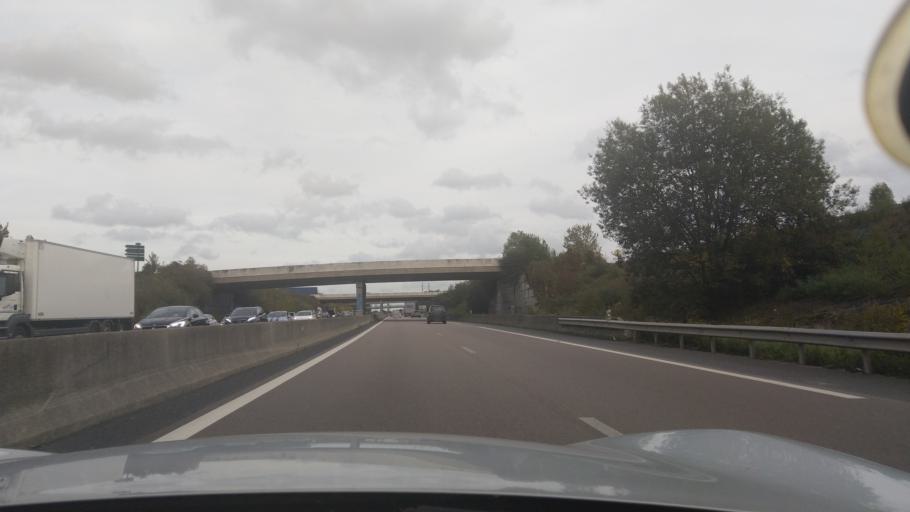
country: FR
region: Ile-de-France
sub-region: Departement du Val-d'Oise
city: Louvres
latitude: 49.0301
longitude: 2.4974
